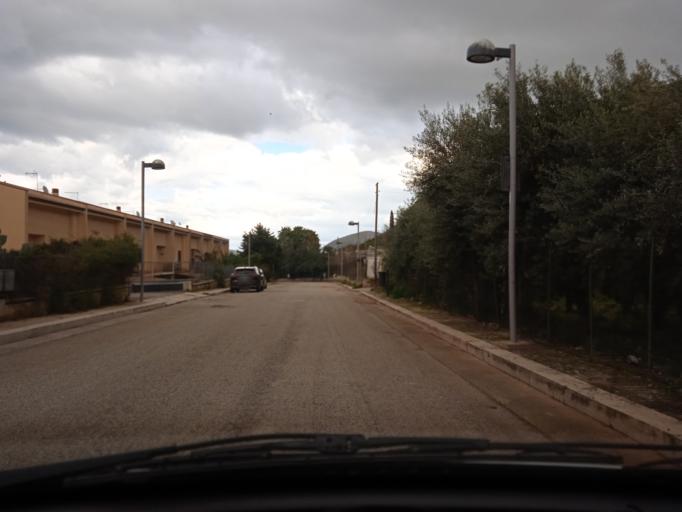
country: IT
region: Sicily
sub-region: Palermo
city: Villabate
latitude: 38.0724
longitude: 13.4400
